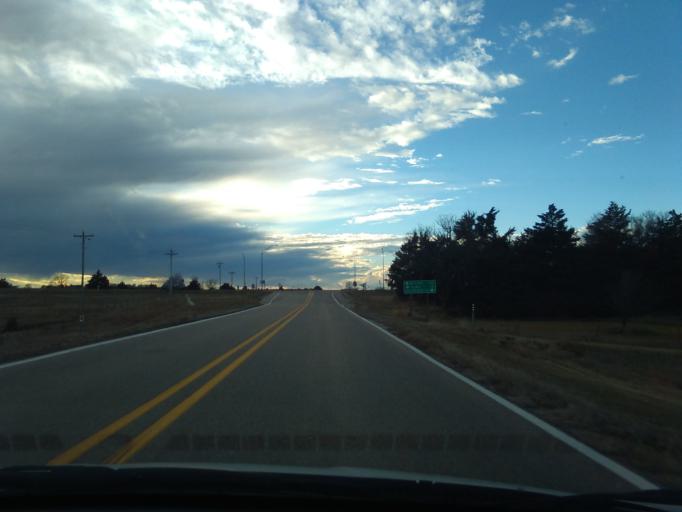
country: US
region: Nebraska
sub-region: Phelps County
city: Holdrege
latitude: 40.3071
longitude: -99.3660
